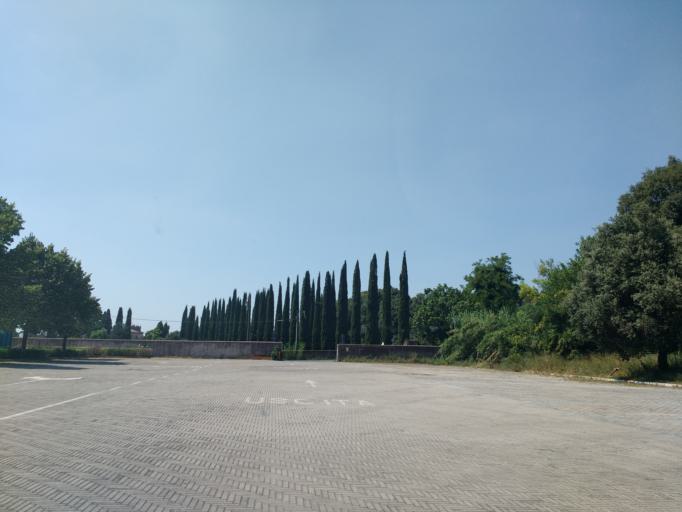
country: IT
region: Latium
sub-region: Citta metropolitana di Roma Capitale
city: Villa Adriana
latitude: 41.9467
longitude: 12.7741
